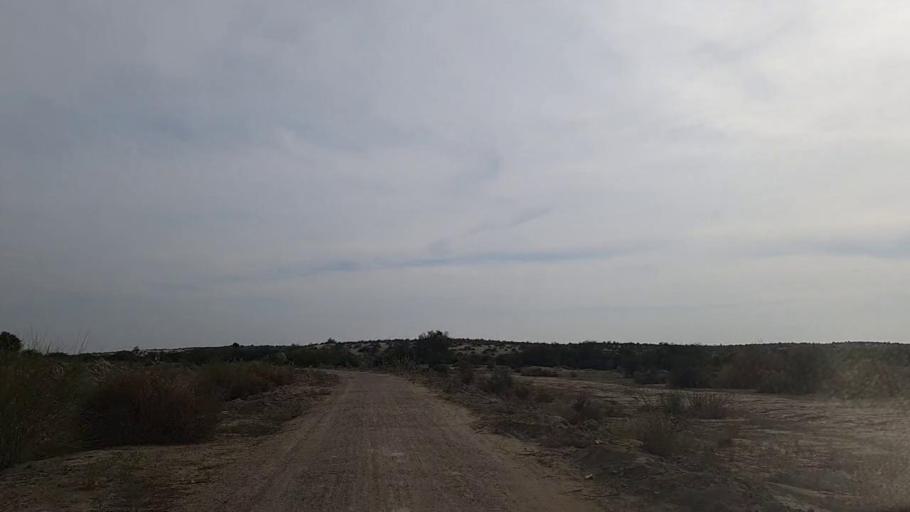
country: PK
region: Sindh
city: Jam Sahib
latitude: 26.4415
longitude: 68.6233
